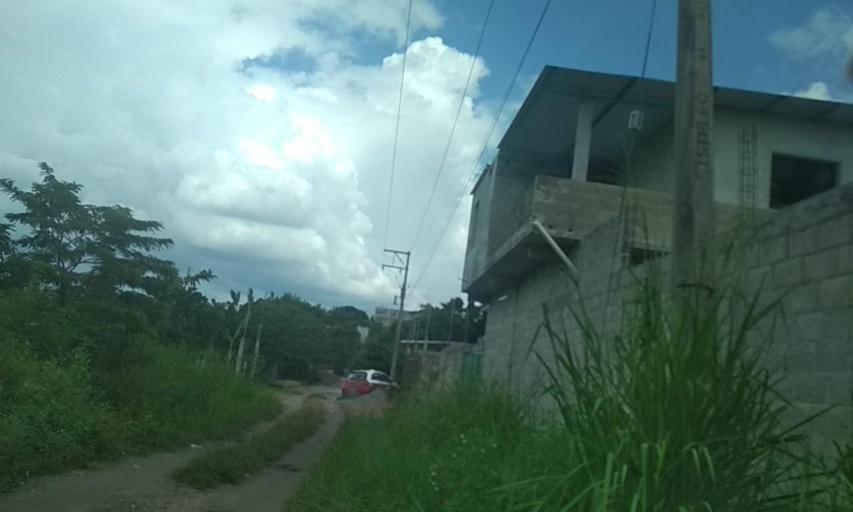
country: MX
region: Veracruz
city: Martinez de la Torre
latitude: 20.0767
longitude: -97.0800
